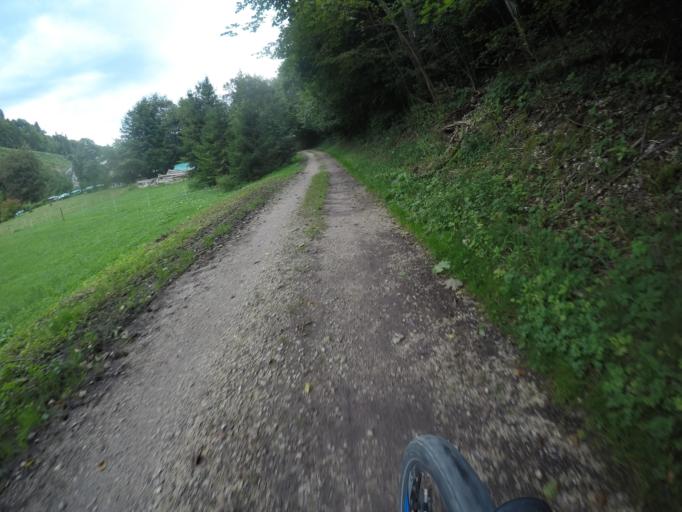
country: DE
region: Baden-Wuerttemberg
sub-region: Tuebingen Region
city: Munsingen
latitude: 48.4467
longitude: 9.4514
